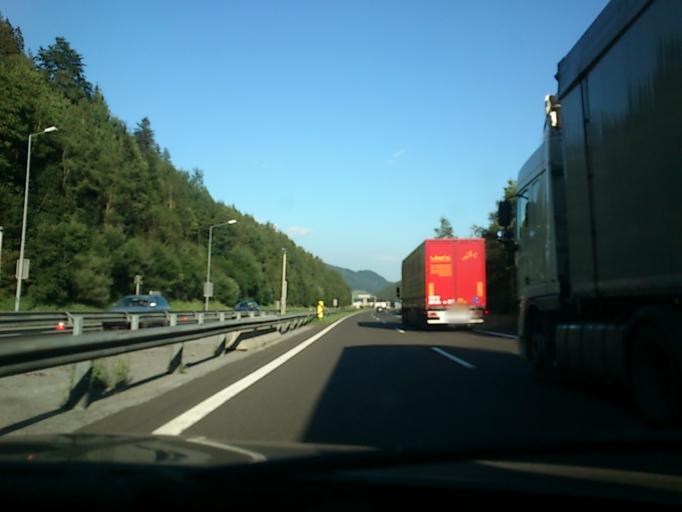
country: AT
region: Styria
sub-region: Politischer Bezirk Leoben
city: Kalwang
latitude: 47.4282
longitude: 14.7151
